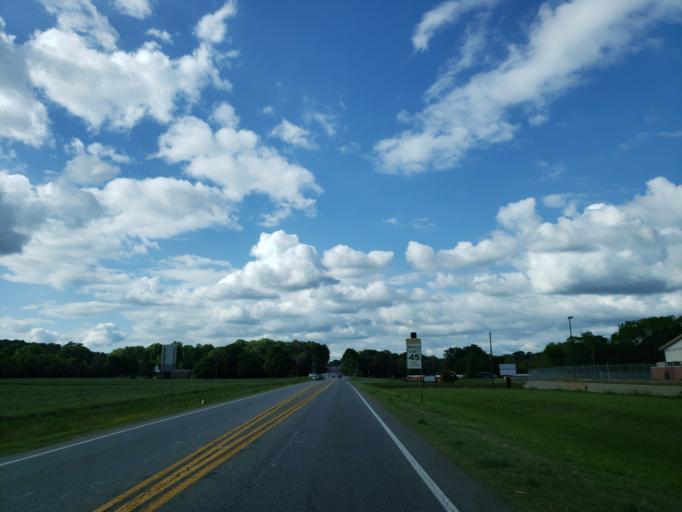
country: US
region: Georgia
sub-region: Bartow County
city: Cartersville
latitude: 34.2414
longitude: -84.8569
